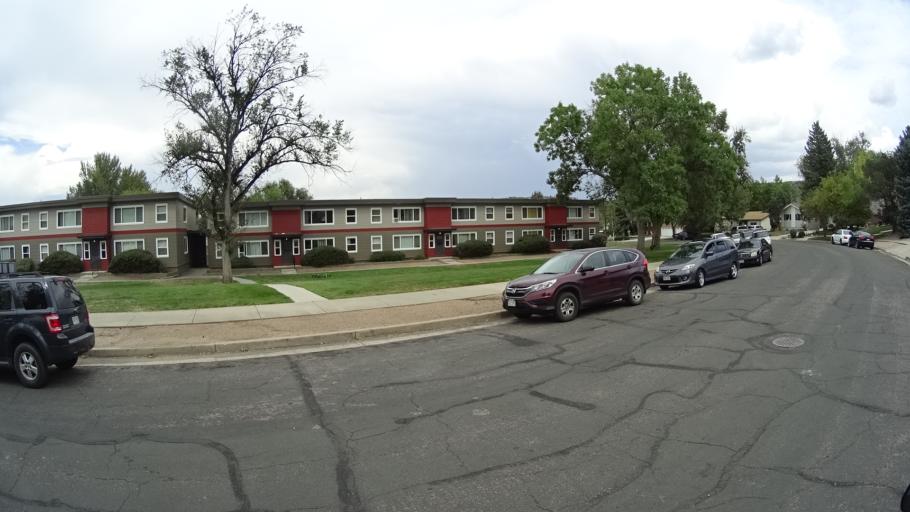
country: US
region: Colorado
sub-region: El Paso County
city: Colorado Springs
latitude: 38.8666
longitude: -104.7893
